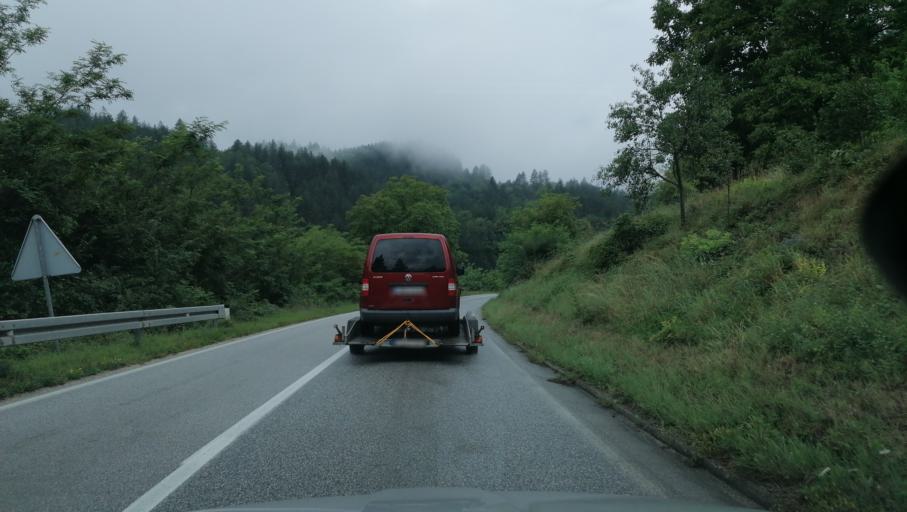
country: RS
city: Durici
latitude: 43.7788
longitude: 19.3674
